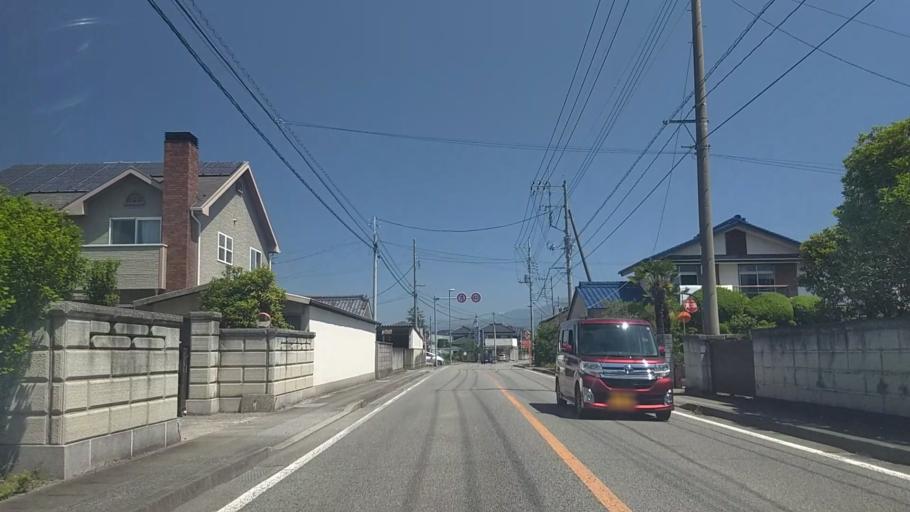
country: JP
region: Yamanashi
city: Ryuo
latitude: 35.6531
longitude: 138.4636
